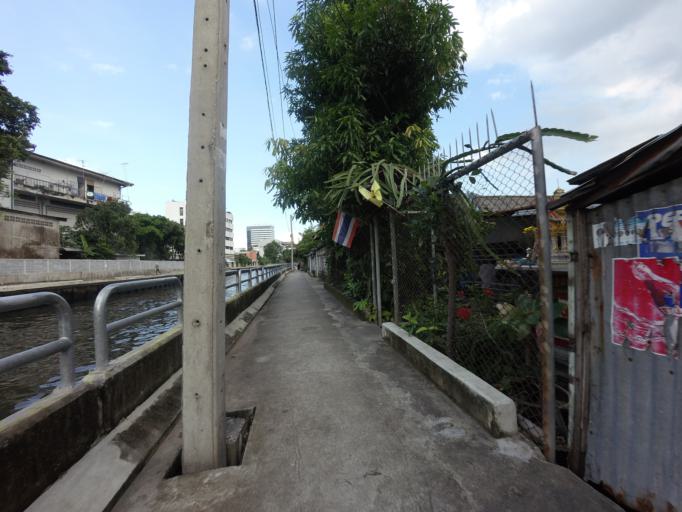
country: TH
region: Bangkok
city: Watthana
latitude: 13.7455
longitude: 100.5746
